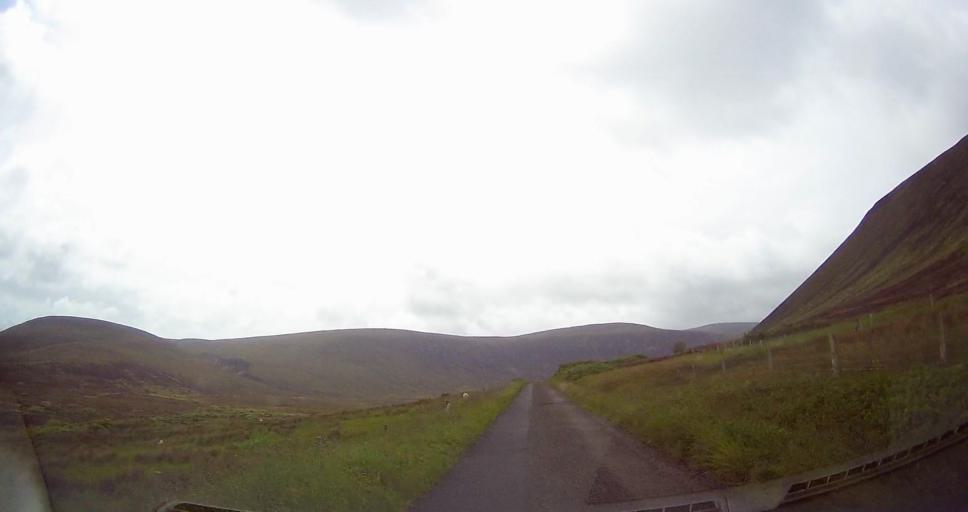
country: GB
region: Scotland
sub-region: Orkney Islands
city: Stromness
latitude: 58.9007
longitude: -3.3153
